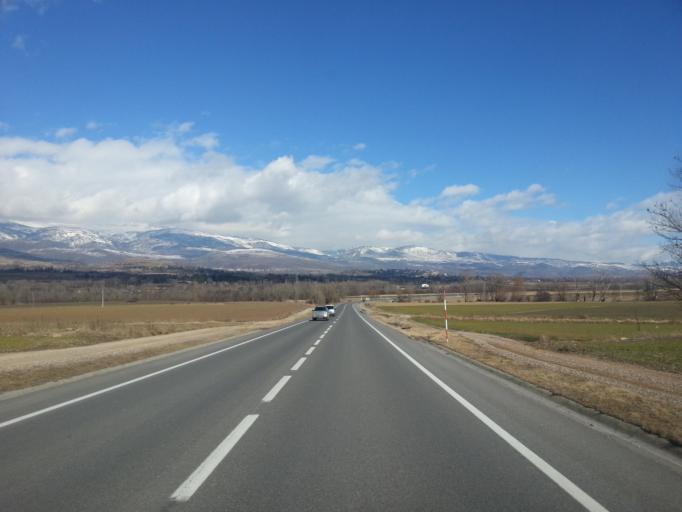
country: ES
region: Catalonia
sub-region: Provincia de Girona
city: Alp
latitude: 42.3906
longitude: 1.8946
